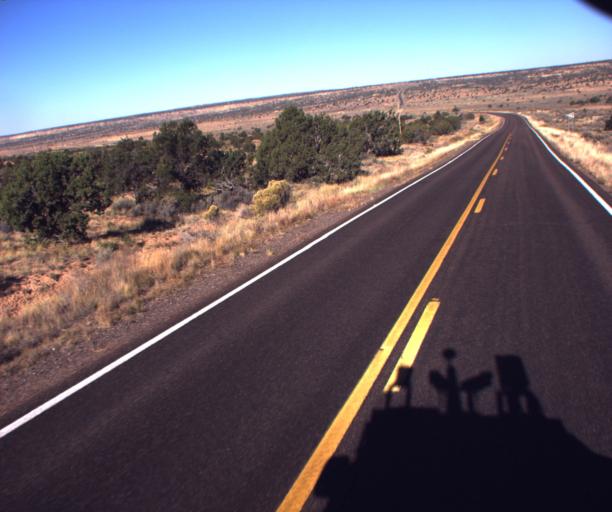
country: US
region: Arizona
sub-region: Navajo County
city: First Mesa
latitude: 35.7454
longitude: -110.1220
